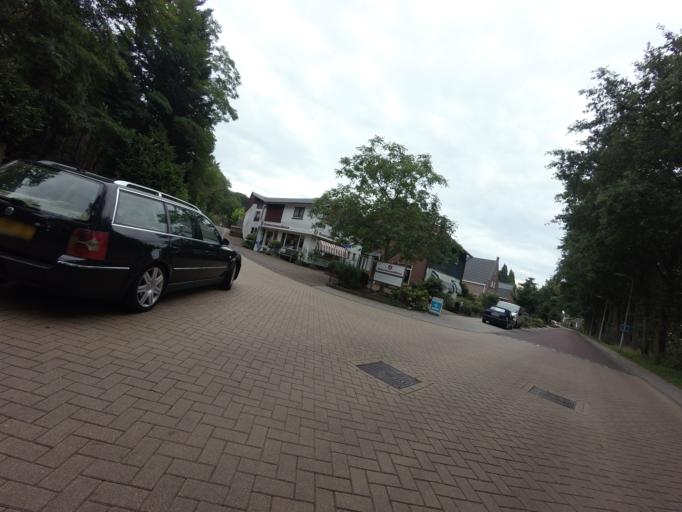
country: NL
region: Overijssel
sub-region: Gemeente Hof van Twente
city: Markelo
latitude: 52.2873
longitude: 6.4125
